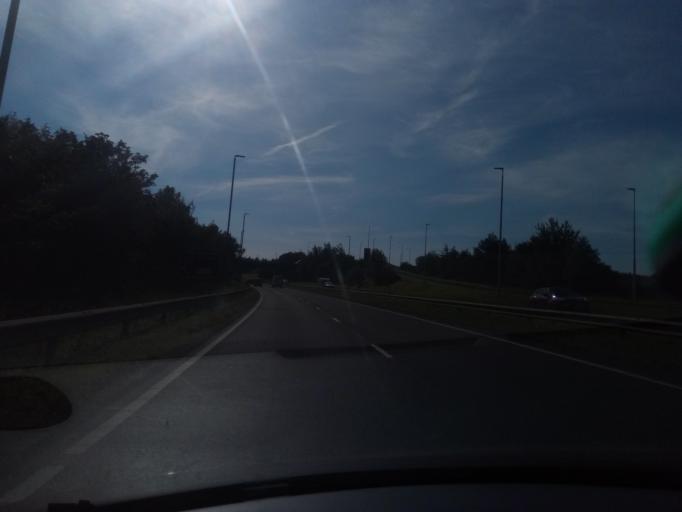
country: GB
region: England
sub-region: County Durham
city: Hawthorn
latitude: 54.8068
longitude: -1.3597
